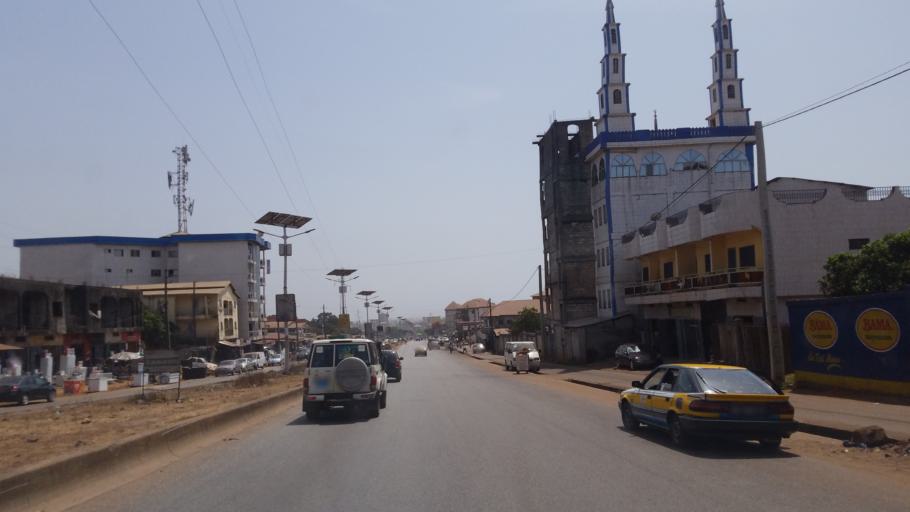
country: GN
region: Conakry
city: Conakry
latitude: 9.5786
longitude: -13.6522
